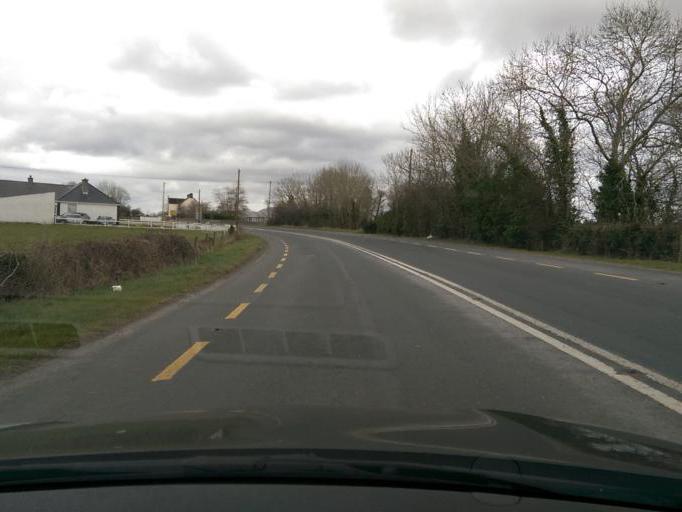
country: IE
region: Leinster
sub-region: An Iarmhi
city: Athlone
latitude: 53.3744
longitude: -8.0088
